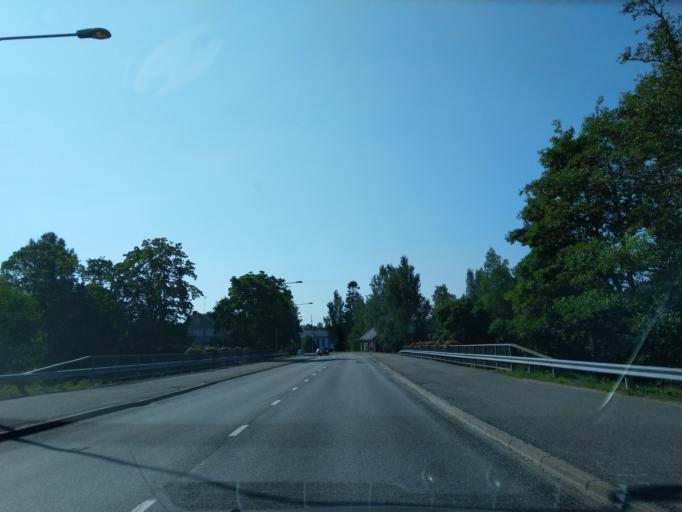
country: FI
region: Satakunta
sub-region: Pori
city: Noormarkku
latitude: 61.5947
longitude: 21.8668
